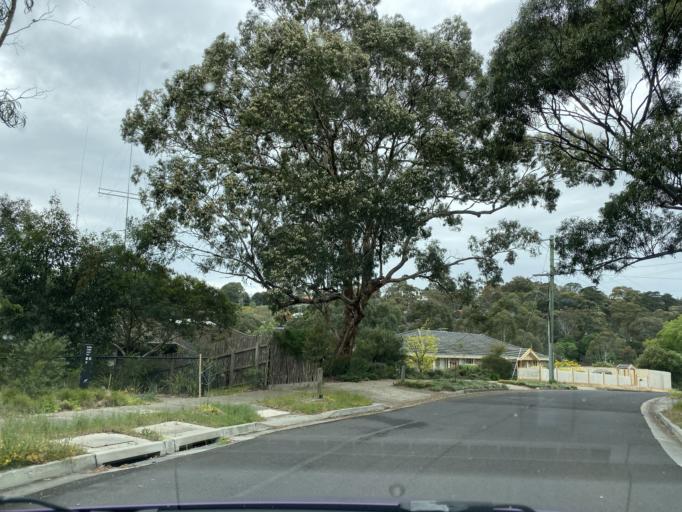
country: AU
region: Victoria
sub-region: Manningham
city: Templestowe Lower
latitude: -37.7611
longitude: 145.1247
